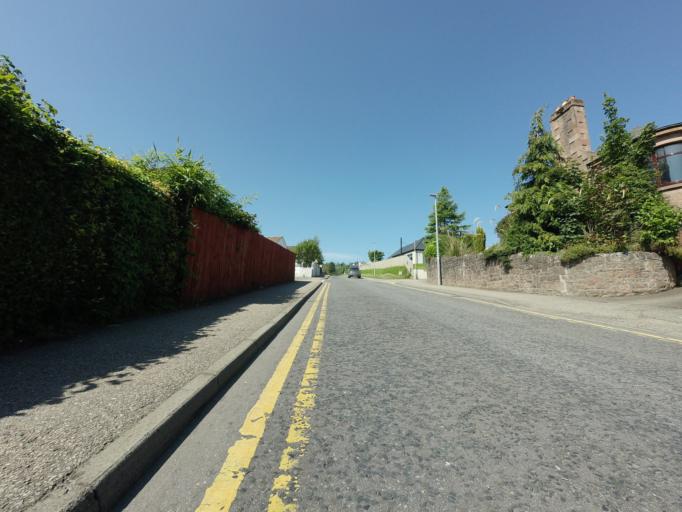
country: GB
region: Scotland
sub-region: Highland
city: Dingwall
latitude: 57.6019
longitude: -4.4292
